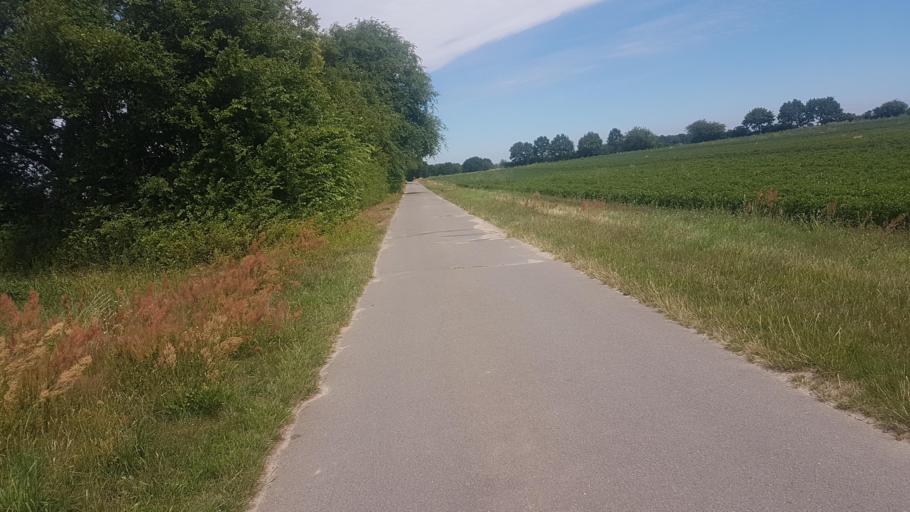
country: DE
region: Lower Saxony
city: Bleckede
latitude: 53.2615
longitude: 10.7628
